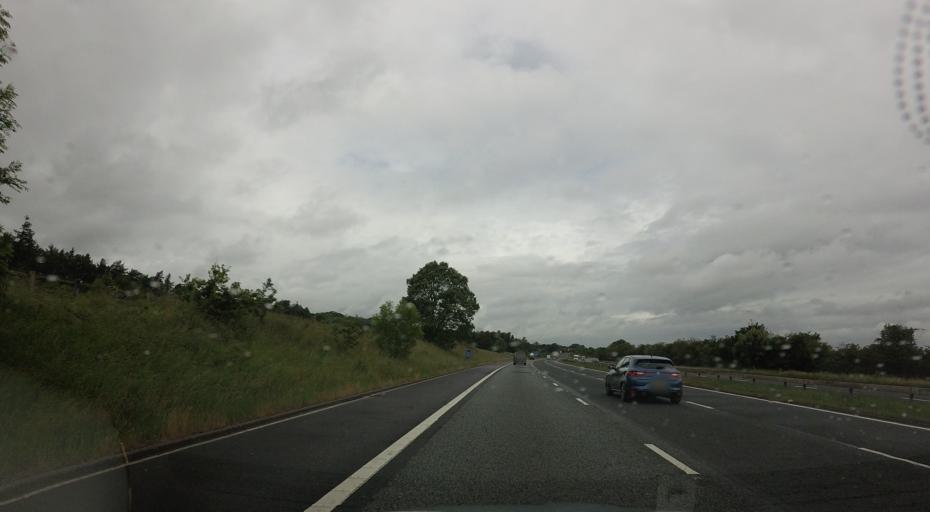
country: GB
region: England
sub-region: Cumbria
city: Scotby
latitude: 54.7901
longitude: -2.8656
